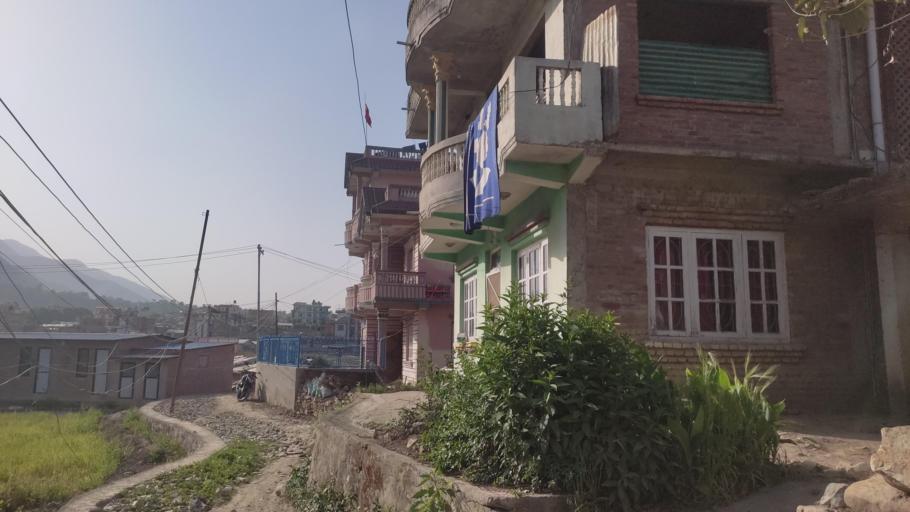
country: NP
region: Central Region
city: Kirtipur
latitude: 27.6601
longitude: 85.2698
